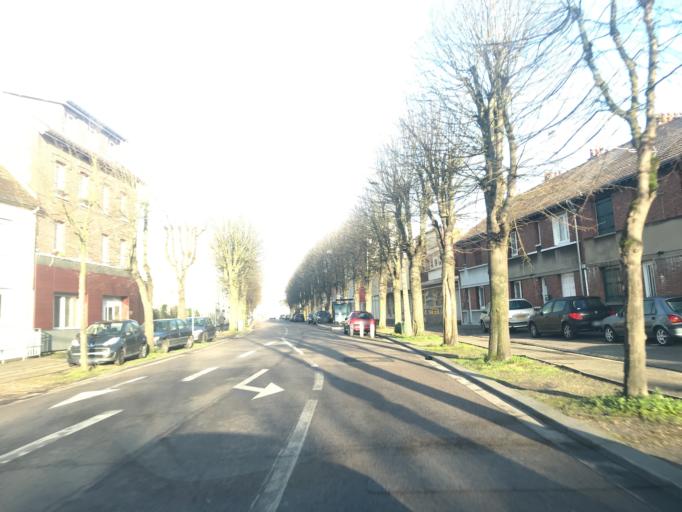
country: FR
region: Haute-Normandie
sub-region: Departement de la Seine-Maritime
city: Sotteville-les-Rouen
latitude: 49.4180
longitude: 1.0973
